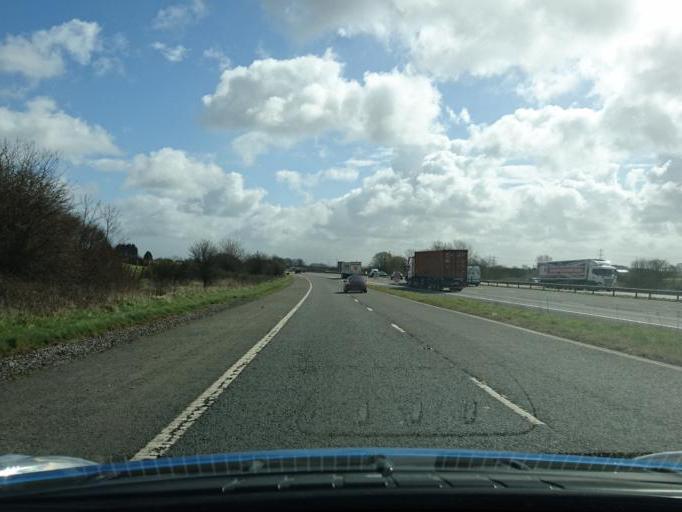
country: GB
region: England
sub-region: South Gloucestershire
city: Hinton
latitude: 51.5020
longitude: -2.3426
